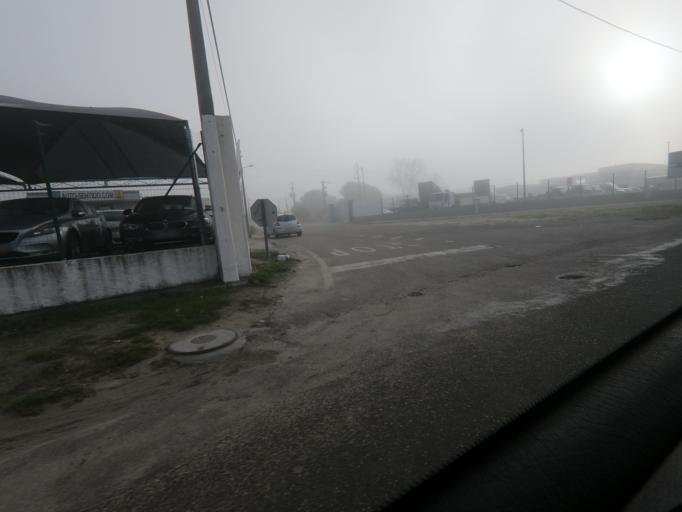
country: PT
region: Setubal
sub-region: Palmela
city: Pinhal Novo
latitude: 38.6127
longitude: -8.9110
